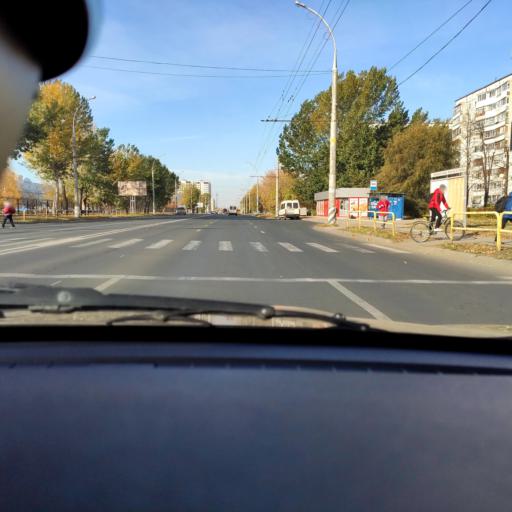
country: RU
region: Samara
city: Tol'yatti
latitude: 53.5077
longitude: 49.2647
